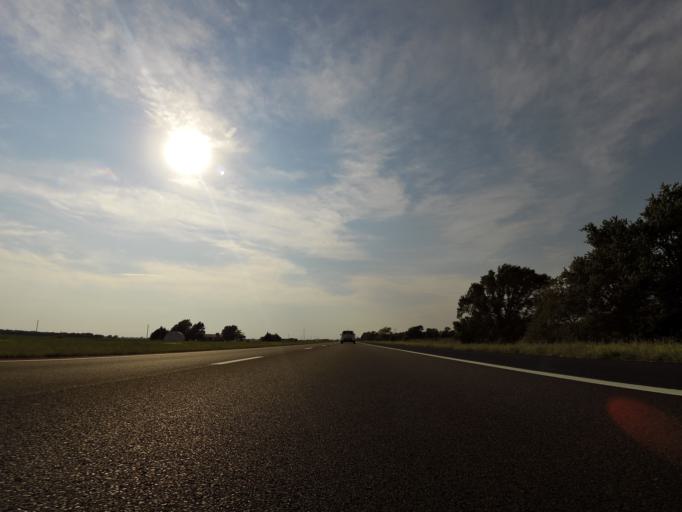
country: US
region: Kansas
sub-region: Reno County
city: Haven
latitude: 37.8891
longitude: -97.7470
